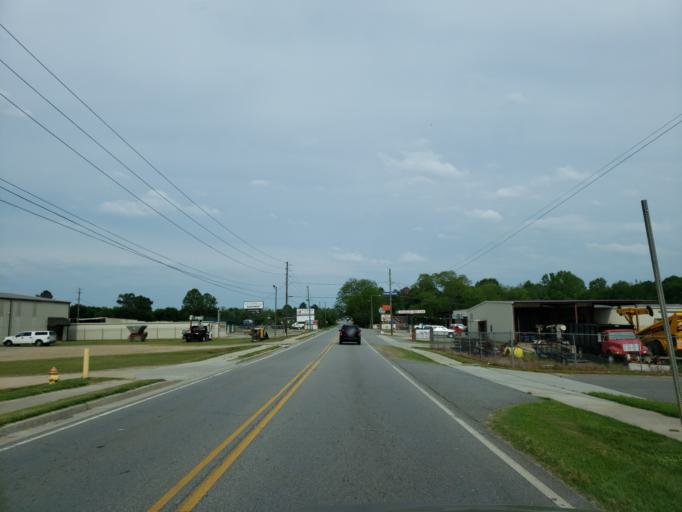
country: US
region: Georgia
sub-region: Dooly County
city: Vienna
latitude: 32.0924
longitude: -83.8042
